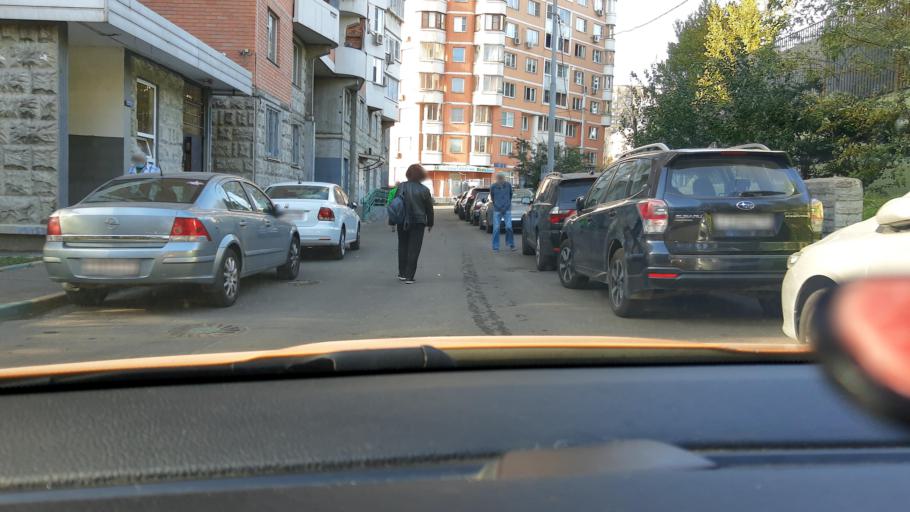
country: RU
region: Moscow
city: Sokol'niki
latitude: 55.7820
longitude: 37.6618
